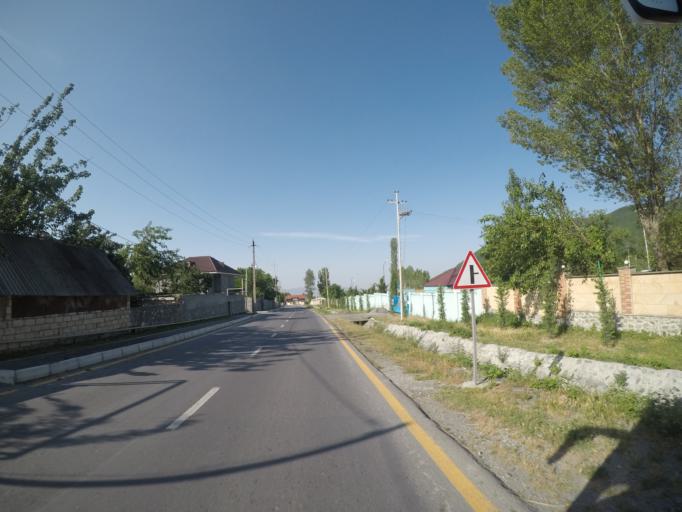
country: AZ
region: Shaki City
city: Sheki
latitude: 41.2269
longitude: 47.1734
